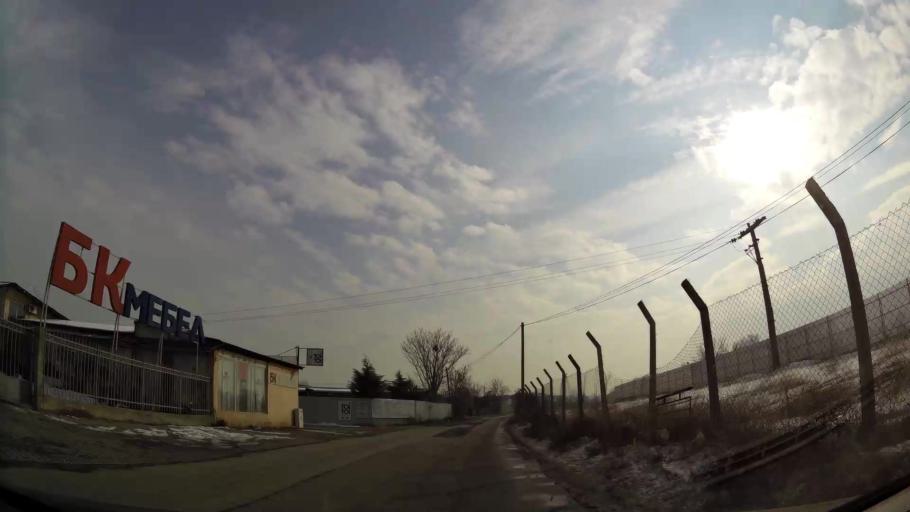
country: MK
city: Krushopek
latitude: 42.0176
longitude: 21.3669
